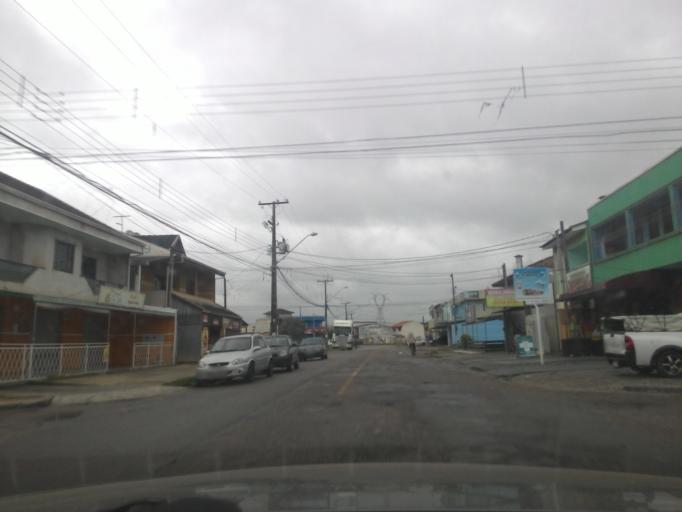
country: BR
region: Parana
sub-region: Araucaria
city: Araucaria
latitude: -25.5426
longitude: -49.3423
